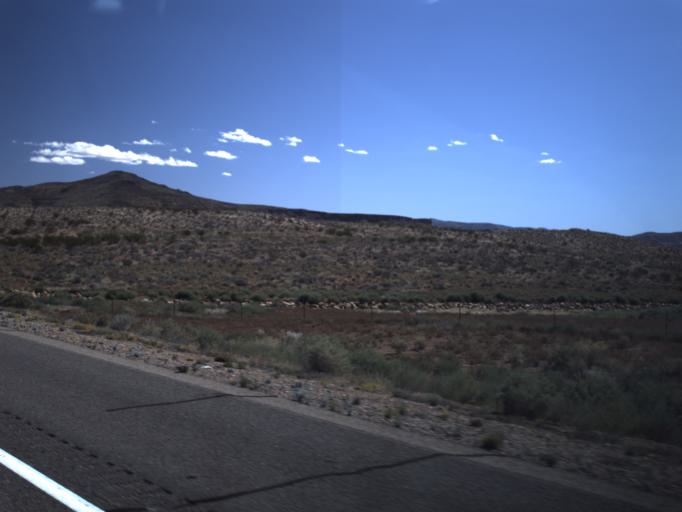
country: US
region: Utah
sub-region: Washington County
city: Saint George
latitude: 37.0046
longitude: -113.5288
